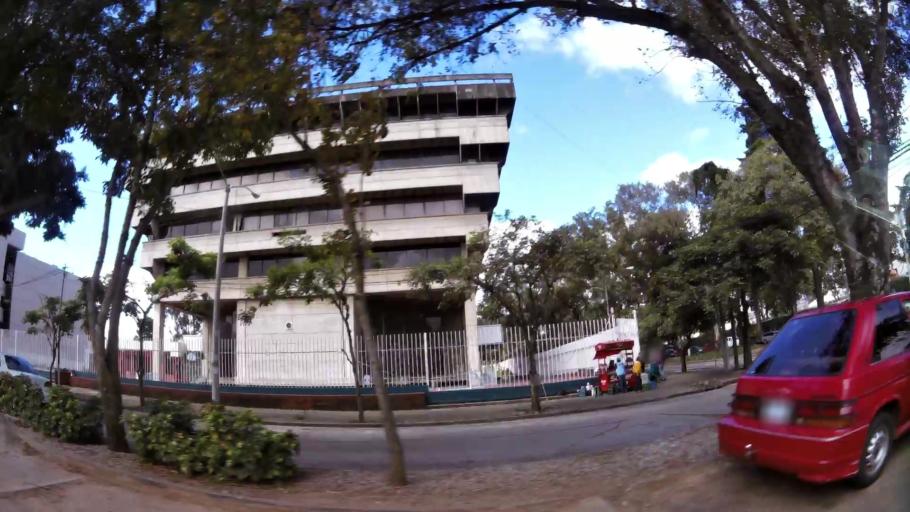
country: GT
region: Guatemala
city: Guatemala City
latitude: 14.6075
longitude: -90.5239
